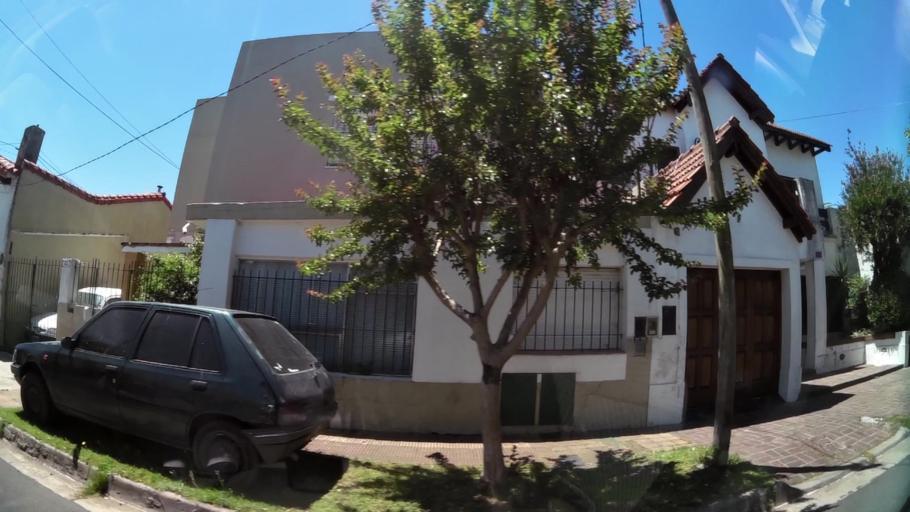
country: AR
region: Buenos Aires
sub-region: Partido de Tigre
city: Tigre
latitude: -34.4433
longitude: -58.5465
